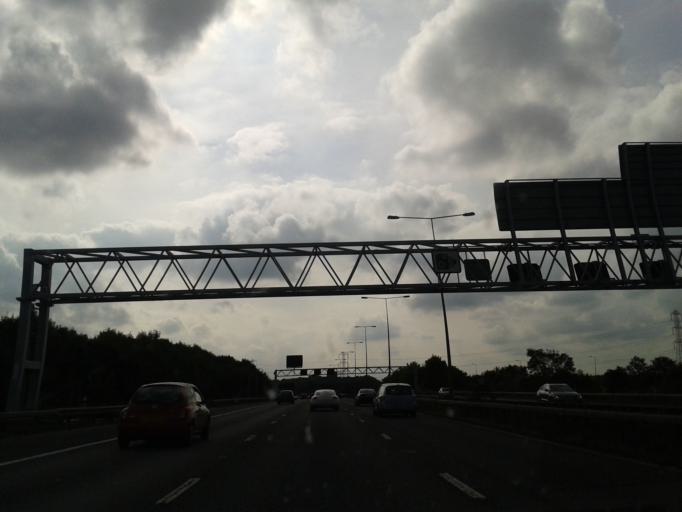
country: GB
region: England
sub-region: Solihull
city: Chelmsley Wood
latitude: 52.4771
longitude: -1.7106
